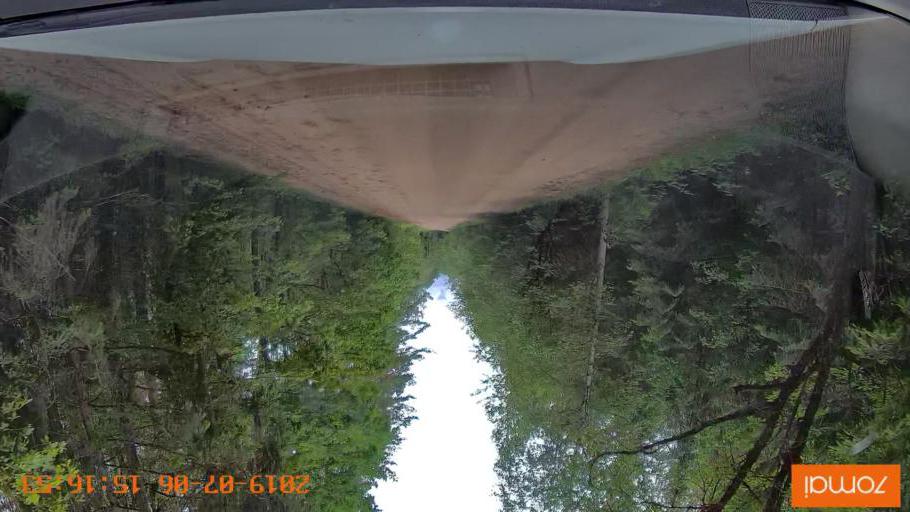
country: BY
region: Minsk
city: Ivyanyets
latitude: 53.9844
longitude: 26.6728
